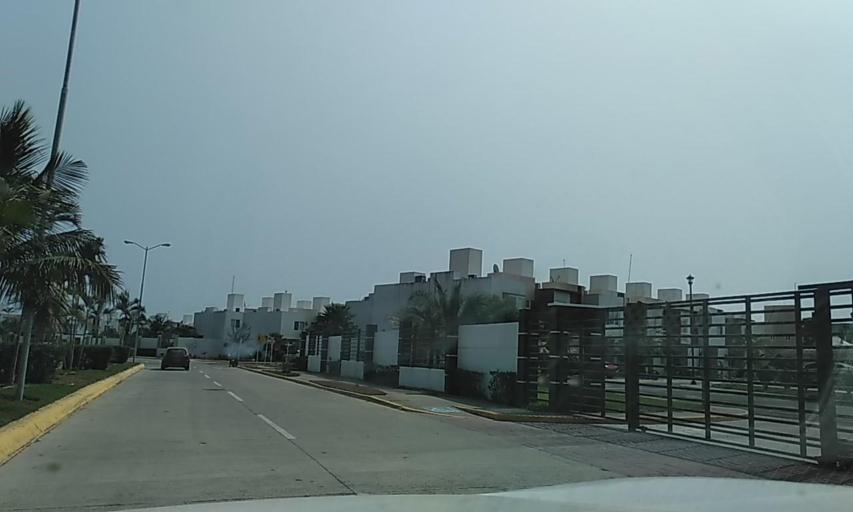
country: MX
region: Veracruz
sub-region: Veracruz
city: Hacienda Sotavento
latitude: 19.1305
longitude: -96.1676
